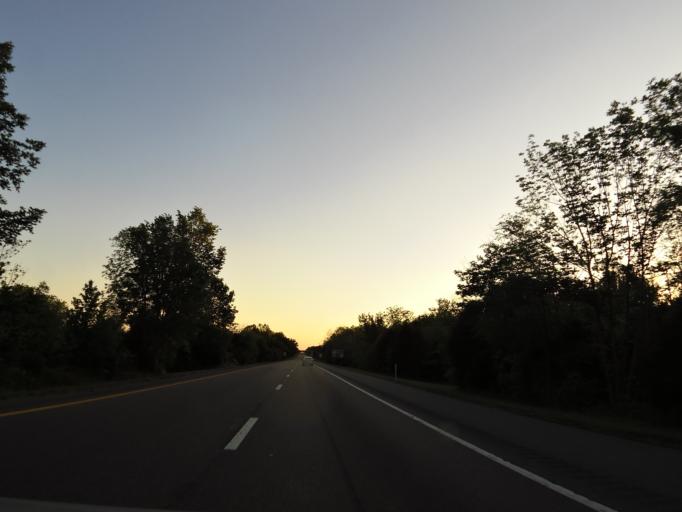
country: US
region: Tennessee
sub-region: Greene County
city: Mosheim
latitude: 36.2340
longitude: -83.0136
